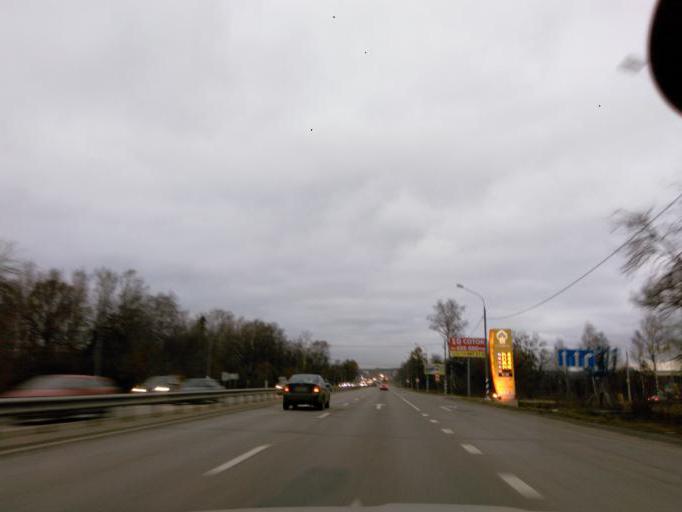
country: RU
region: Moskovskaya
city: Chashnikovo
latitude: 56.0385
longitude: 37.1621
